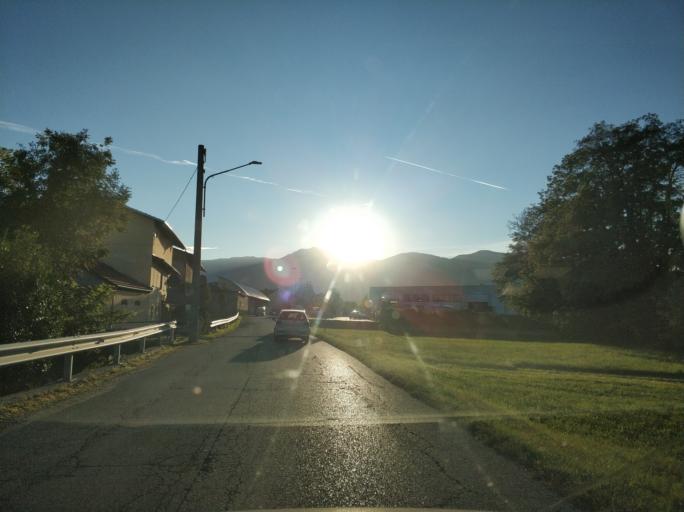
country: IT
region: Piedmont
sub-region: Provincia di Torino
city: Nole
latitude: 45.2428
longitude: 7.5614
